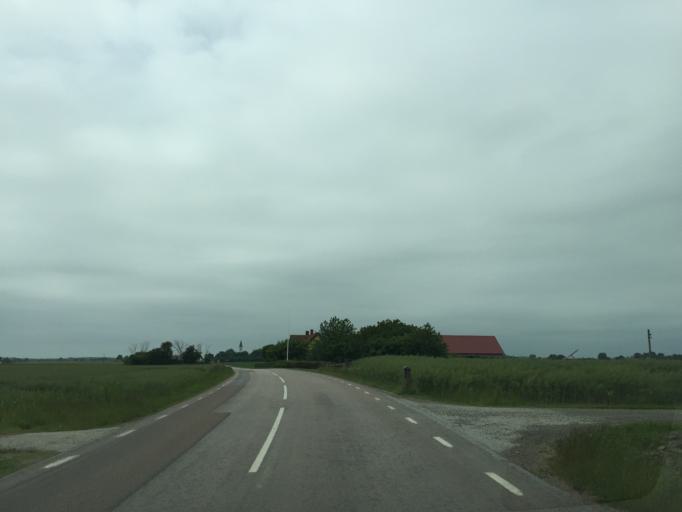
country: SE
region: Skane
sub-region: Ystads Kommun
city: Kopingebro
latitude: 55.4295
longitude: 14.0826
